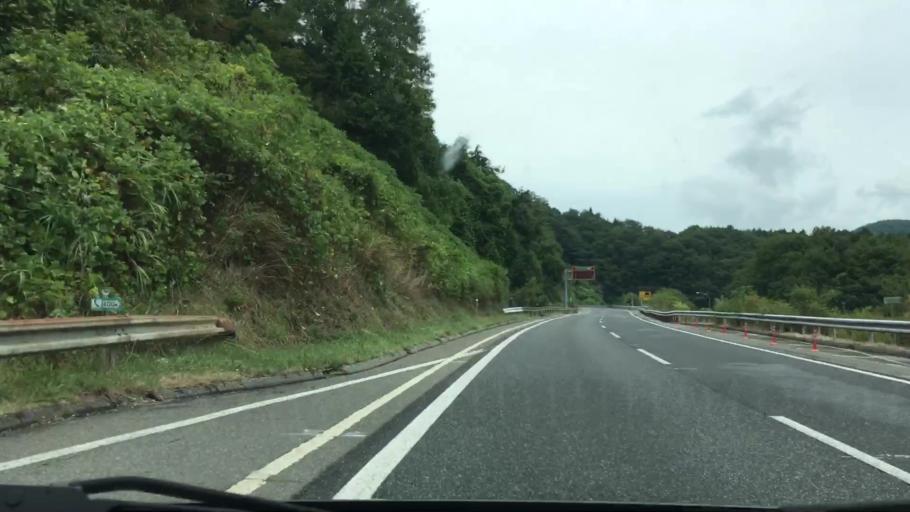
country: JP
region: Okayama
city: Niimi
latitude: 34.9805
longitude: 133.6156
